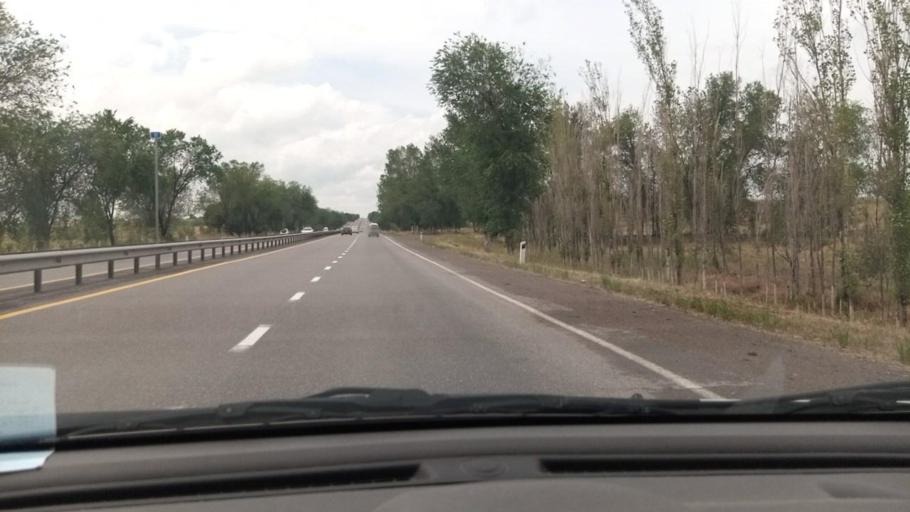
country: UZ
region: Toshkent
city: Ohangaron
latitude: 41.0006
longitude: 69.5265
